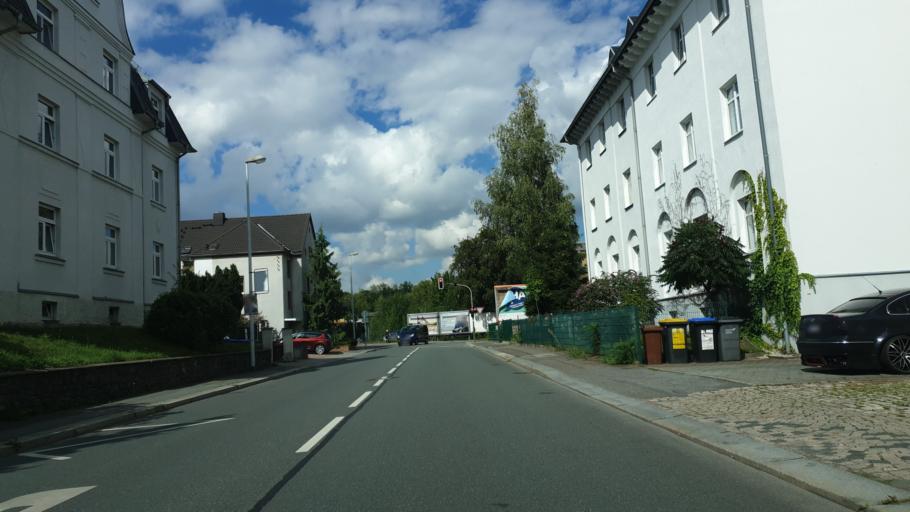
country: DE
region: Saxony
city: Neukirchen
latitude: 50.8184
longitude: 12.8706
